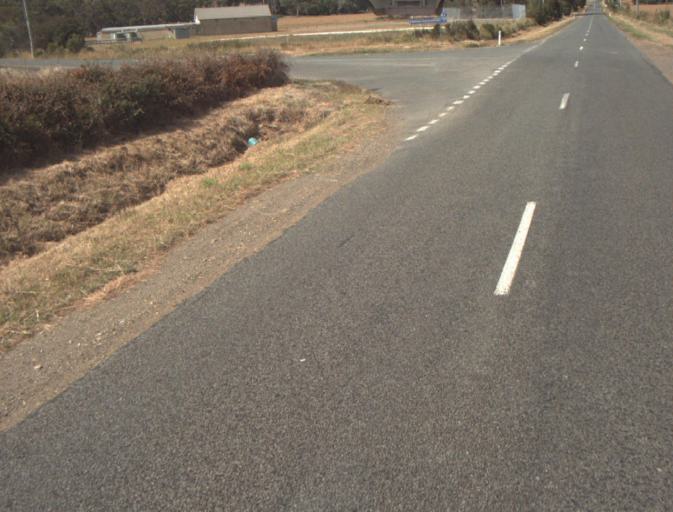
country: AU
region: Tasmania
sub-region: Launceston
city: Mayfield
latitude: -41.2523
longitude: 147.1474
